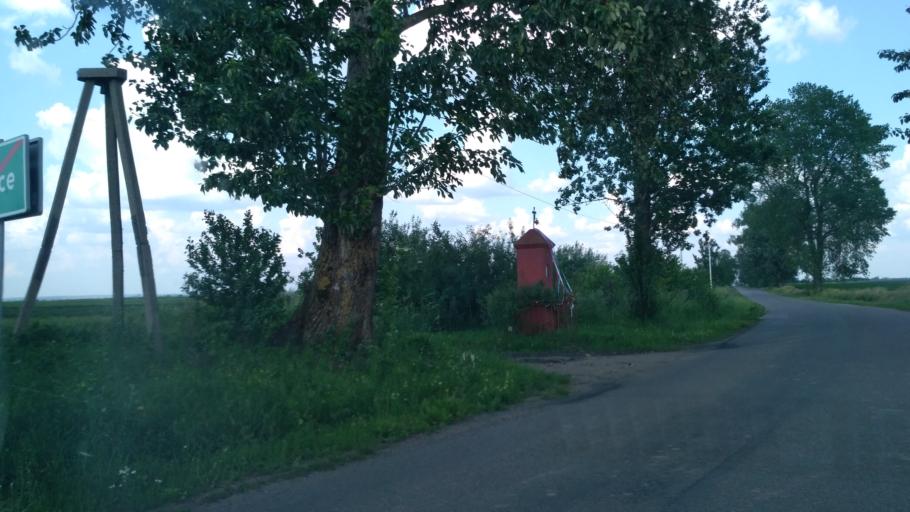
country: PL
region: Subcarpathian Voivodeship
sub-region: Powiat jaroslawski
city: Ostrow
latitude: 49.9433
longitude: 22.7606
